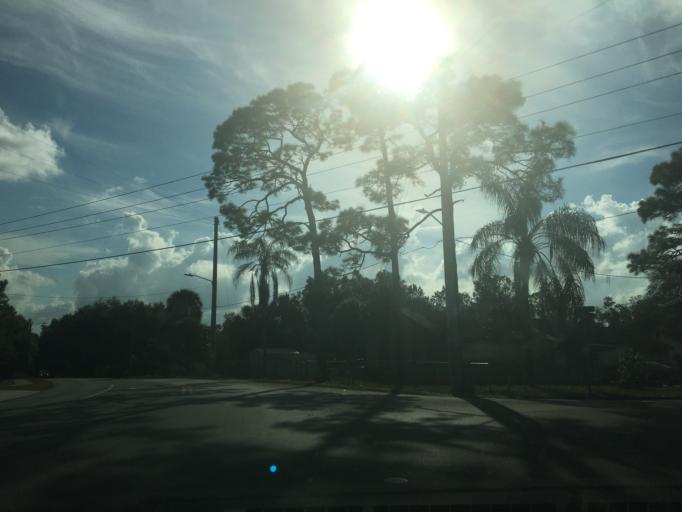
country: US
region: Florida
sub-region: Hillsborough County
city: University
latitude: 28.0254
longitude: -82.4346
